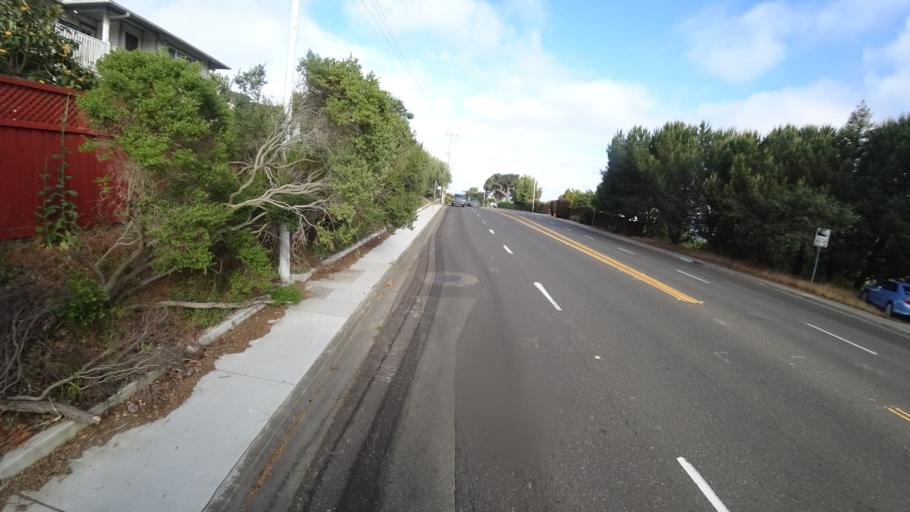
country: US
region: California
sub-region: Alameda County
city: Fairview
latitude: 37.6557
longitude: -122.0374
